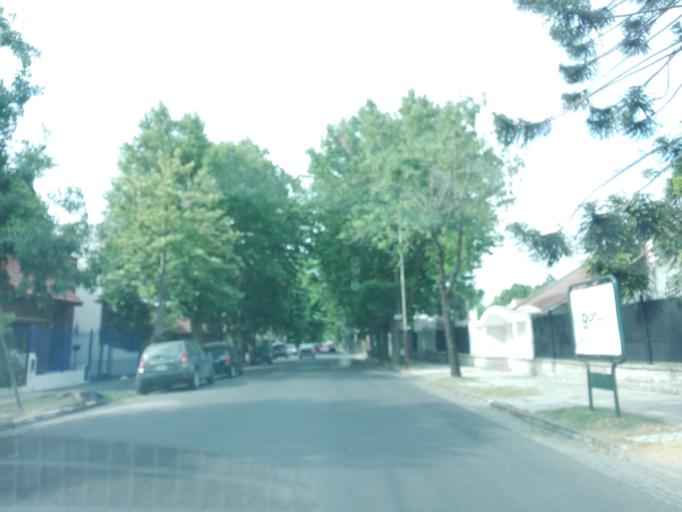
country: AR
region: Buenos Aires
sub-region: Partido de Lomas de Zamora
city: Lomas de Zamora
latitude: -34.7514
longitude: -58.3976
